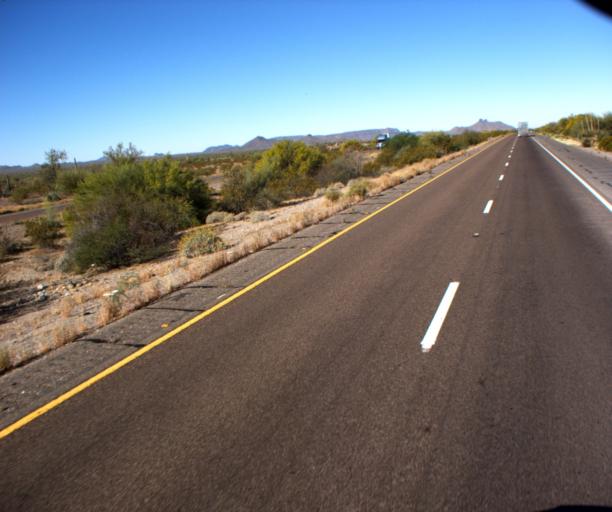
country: US
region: Arizona
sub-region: Pinal County
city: Maricopa
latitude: 32.8502
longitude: -112.3459
